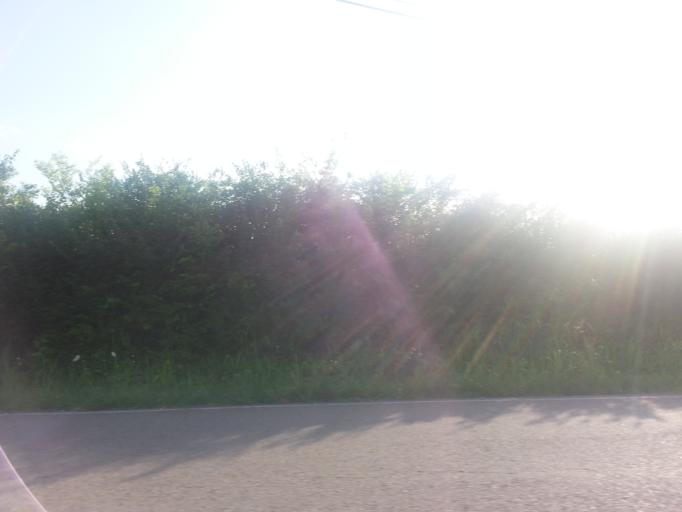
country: US
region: Tennessee
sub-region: Knox County
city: Knoxville
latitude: 35.8830
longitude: -83.8992
